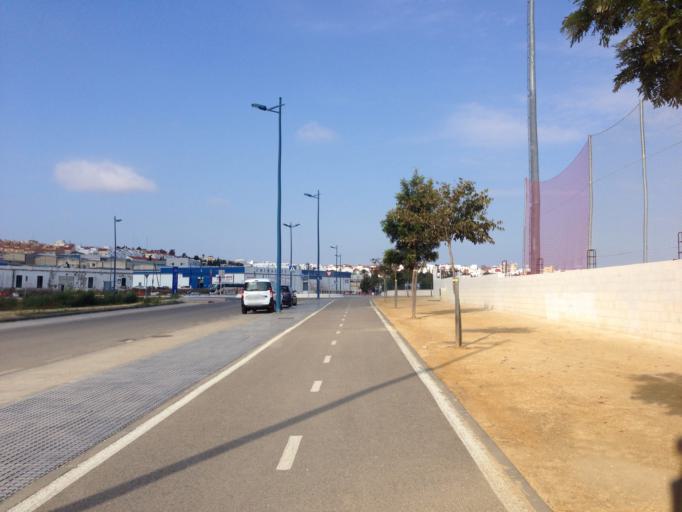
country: ES
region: Andalusia
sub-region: Provincia de Cadiz
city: Chiclana de la Frontera
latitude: 36.4114
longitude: -6.1370
